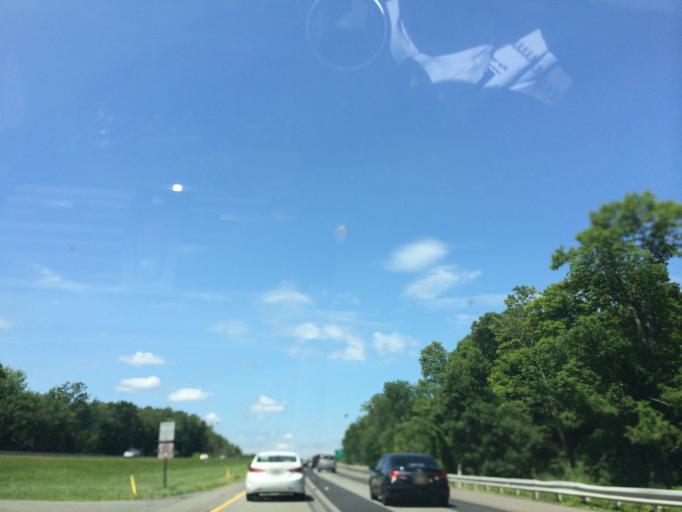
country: US
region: Pennsylvania
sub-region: Wayne County
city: Hawley
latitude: 41.3598
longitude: -75.1928
